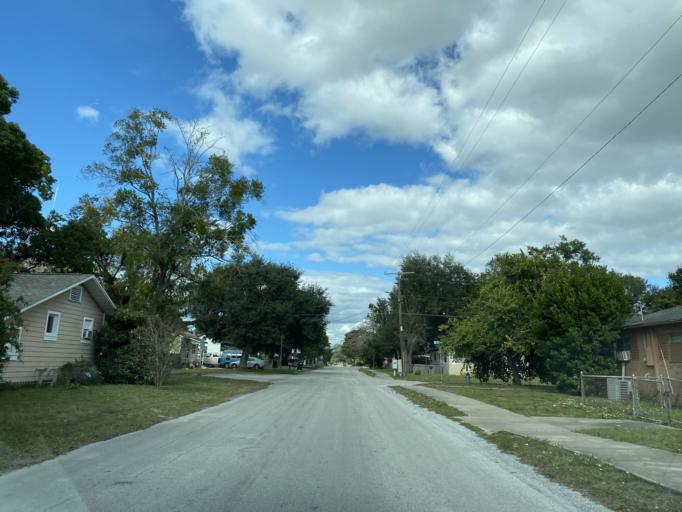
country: US
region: Florida
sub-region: Orange County
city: Orlando
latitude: 28.5188
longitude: -81.3888
